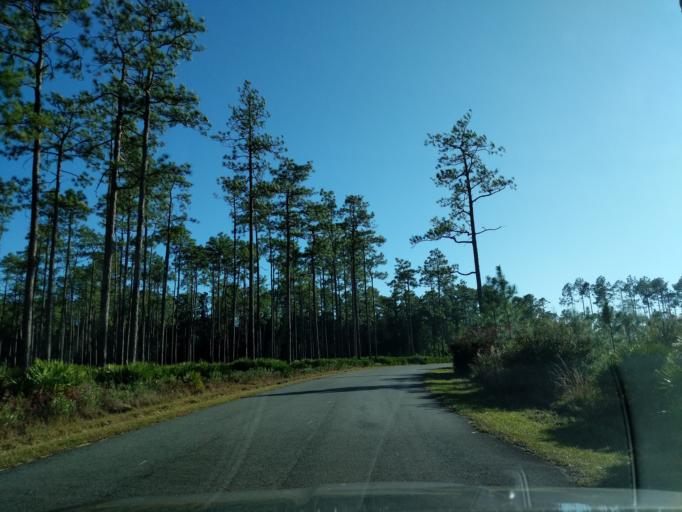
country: US
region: Georgia
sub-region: Charlton County
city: Folkston
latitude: 30.7363
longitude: -82.1362
